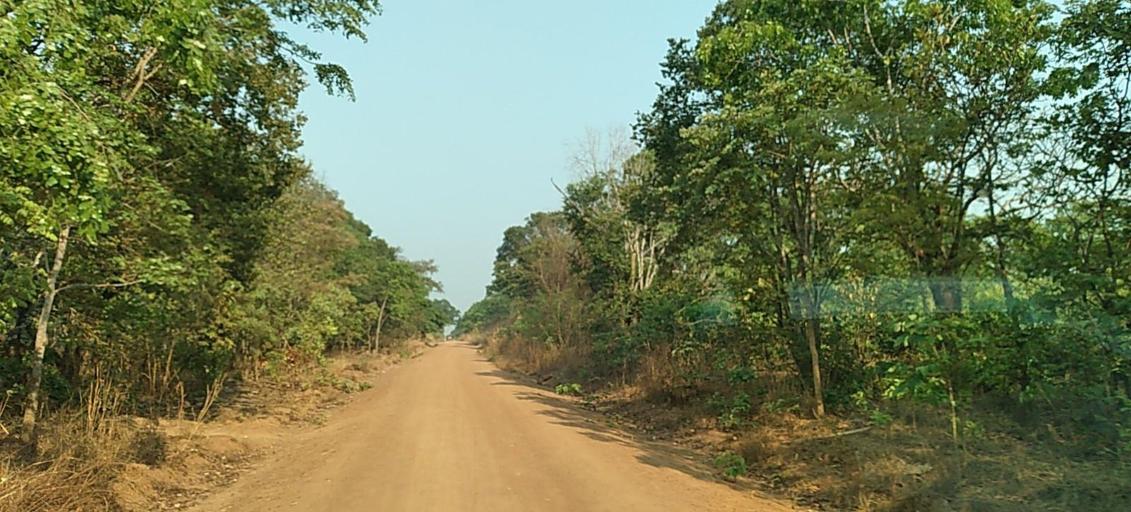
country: ZM
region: Copperbelt
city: Chingola
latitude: -12.8609
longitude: 27.5737
